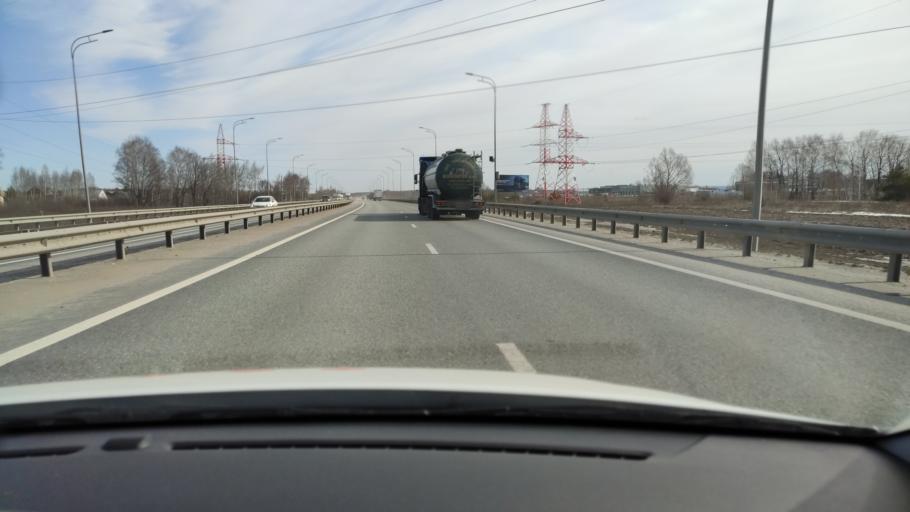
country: RU
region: Tatarstan
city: Osinovo
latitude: 55.9021
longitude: 48.9455
